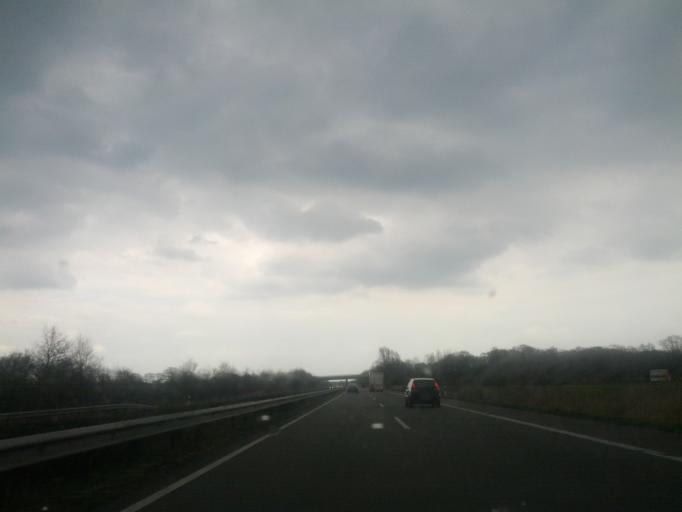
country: DE
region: Lower Saxony
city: Filsum
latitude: 53.2469
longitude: 7.6647
